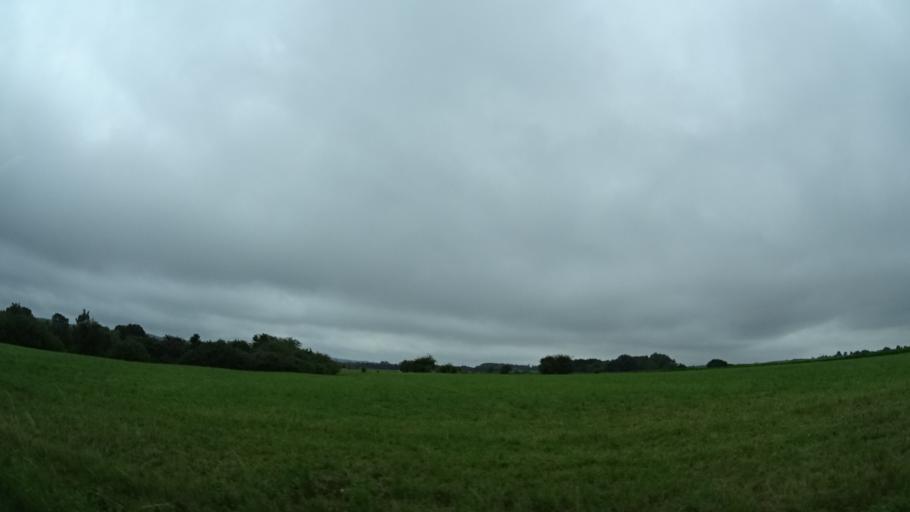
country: BE
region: Wallonia
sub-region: Province du Luxembourg
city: Attert
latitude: 49.7073
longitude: 5.7132
